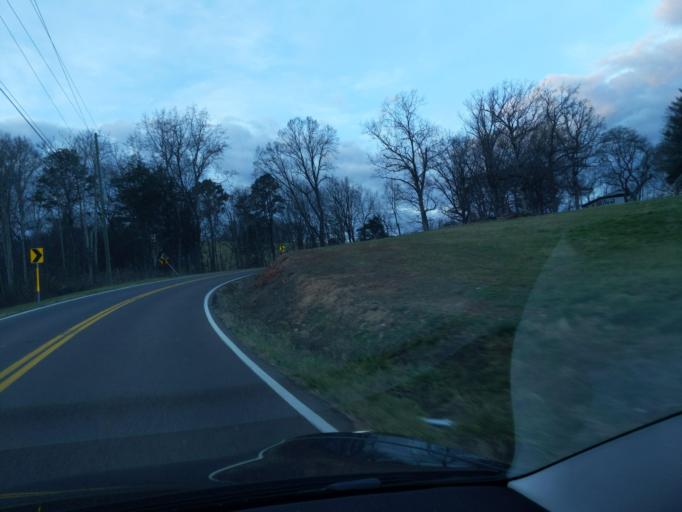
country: US
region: Tennessee
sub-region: Jefferson County
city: White Pine
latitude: 36.1062
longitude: -83.3485
